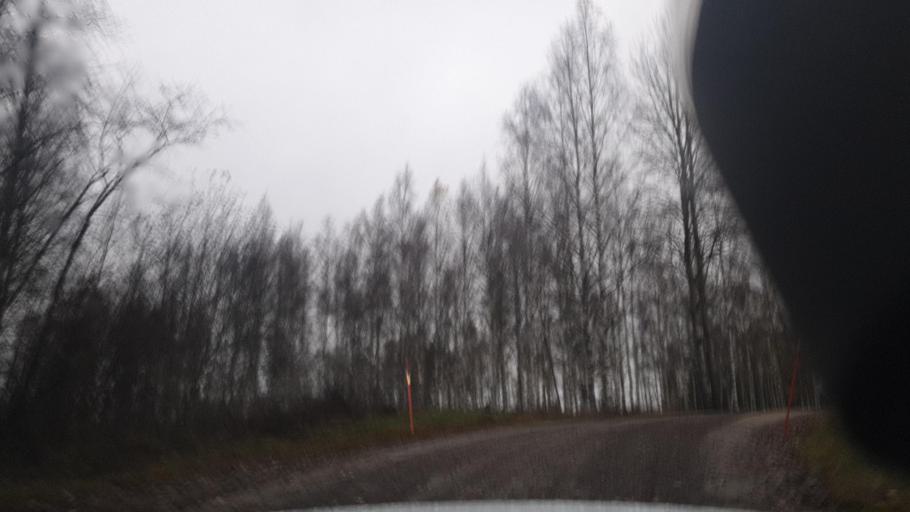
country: SE
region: Vaermland
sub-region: Eda Kommun
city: Charlottenberg
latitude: 59.7337
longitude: 12.1463
